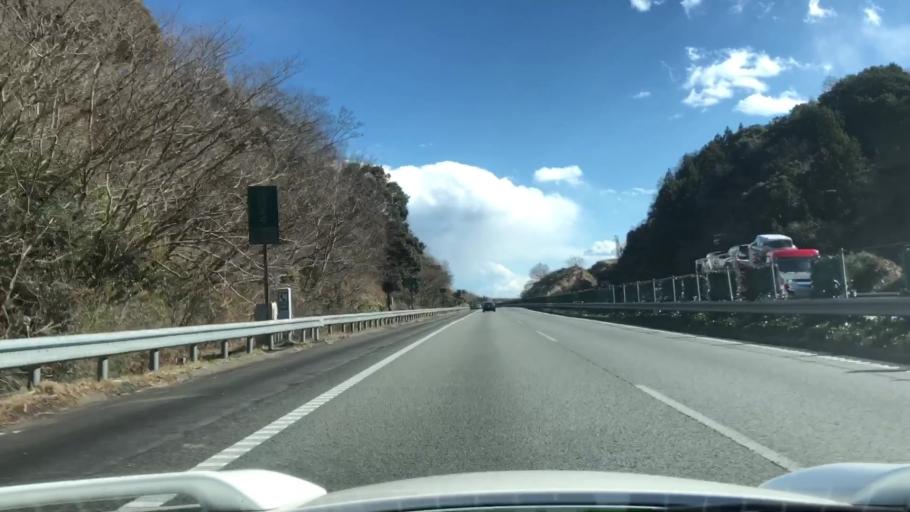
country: JP
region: Shizuoka
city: Kakegawa
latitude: 34.7593
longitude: 138.0514
